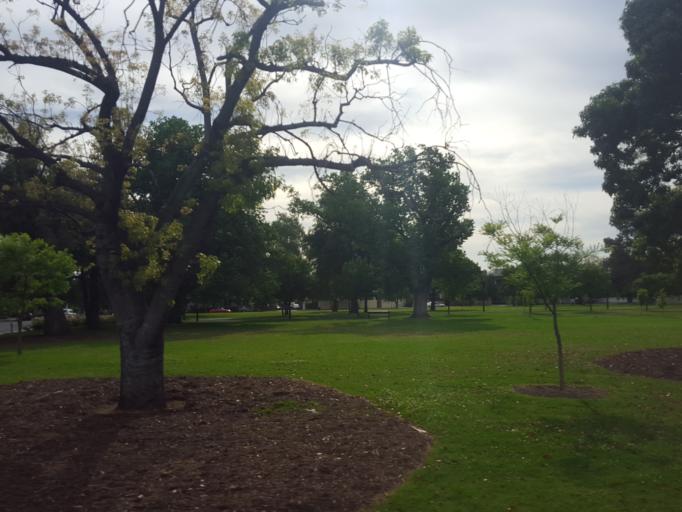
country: AU
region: South Australia
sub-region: Adelaide
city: North Adelaide
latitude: -34.9080
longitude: 138.5925
